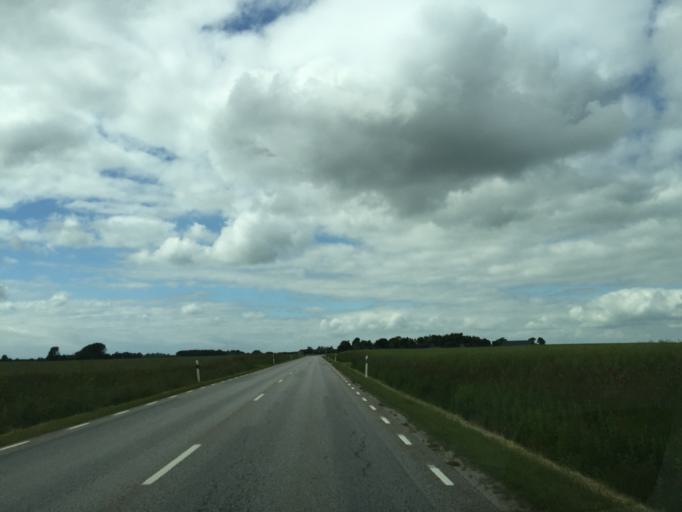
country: SE
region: Skane
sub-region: Svedala Kommun
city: Klagerup
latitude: 55.6242
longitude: 13.2523
